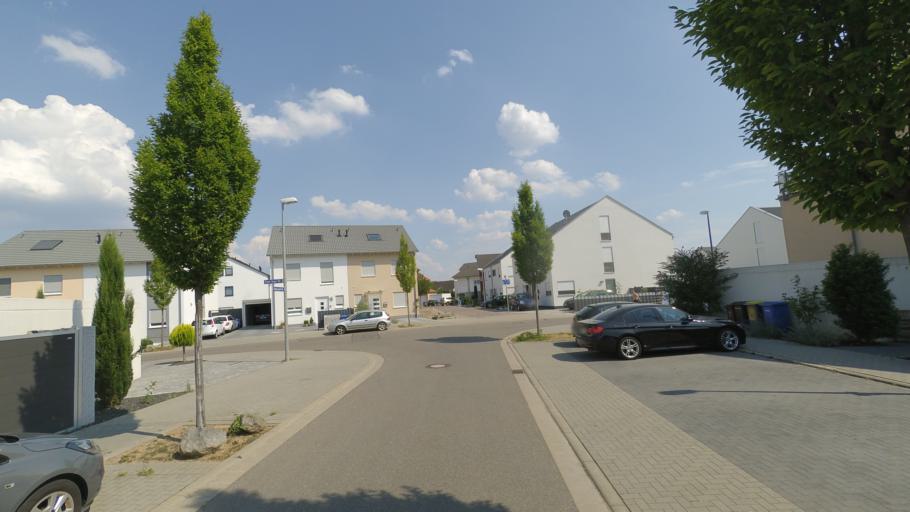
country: DE
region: Rheinland-Pfalz
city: Frankenthal
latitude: 49.5100
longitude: 8.3807
